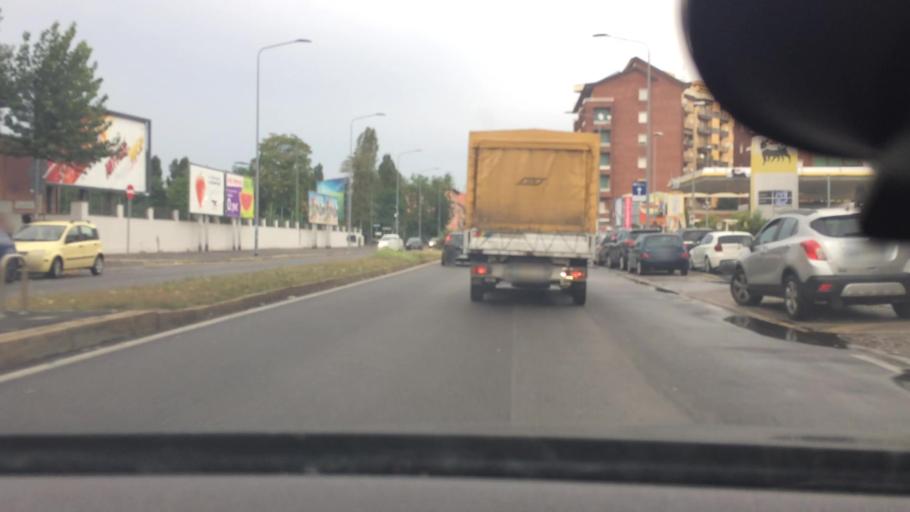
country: IT
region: Lombardy
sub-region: Citta metropolitana di Milano
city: Sesto San Giovanni
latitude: 45.5067
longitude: 9.2230
